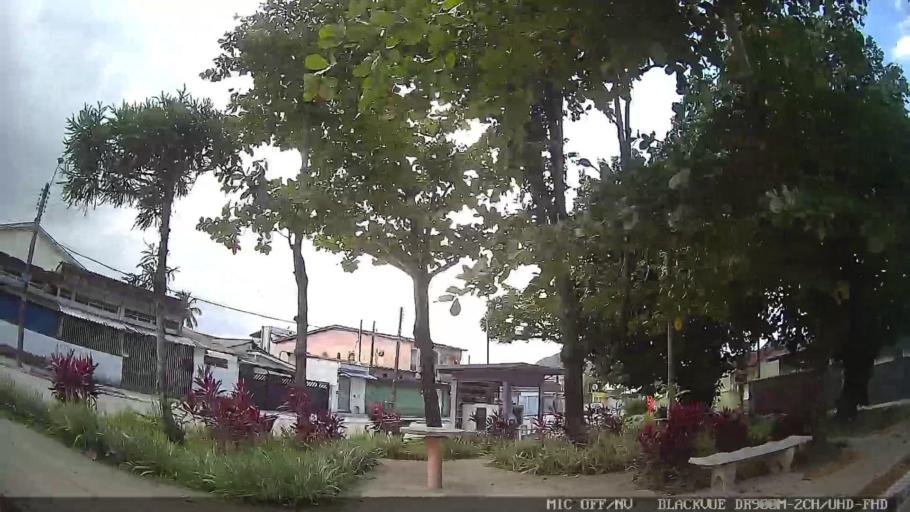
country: BR
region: Sao Paulo
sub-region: Guaruja
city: Guaruja
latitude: -23.9965
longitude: -46.2833
